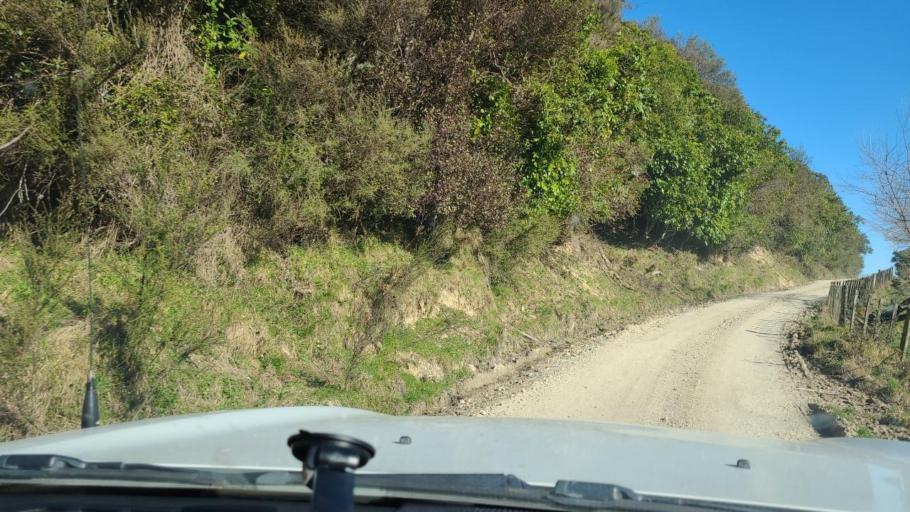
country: NZ
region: Hawke's Bay
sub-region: Wairoa District
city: Wairoa
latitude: -38.6720
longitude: 177.4718
